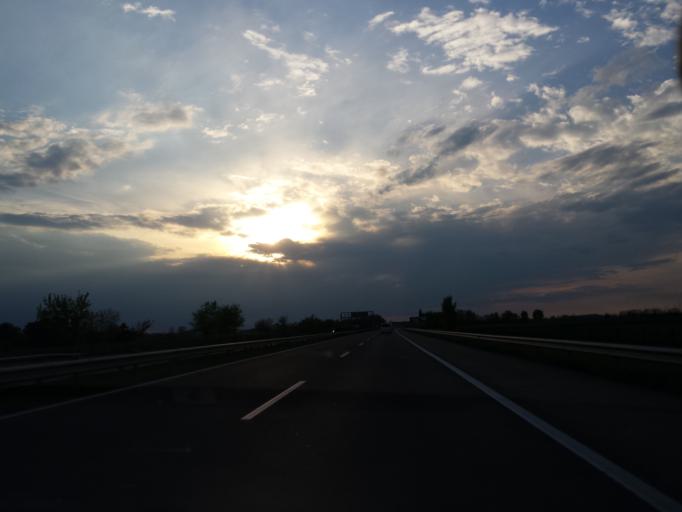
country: HU
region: Gyor-Moson-Sopron
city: Abda
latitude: 47.6900
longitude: 17.5263
